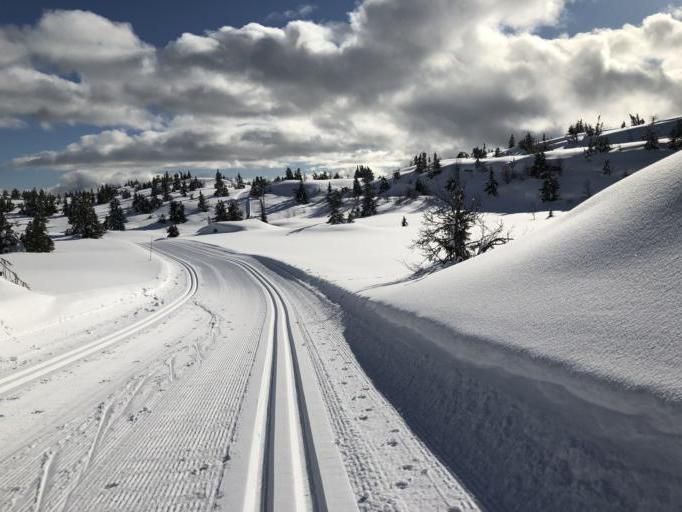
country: NO
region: Oppland
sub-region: Gausdal
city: Segalstad bru
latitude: 61.3306
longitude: 10.0328
